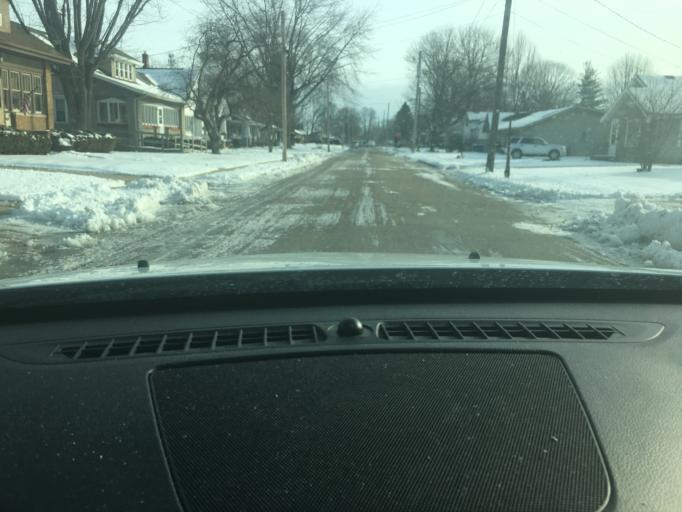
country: US
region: Illinois
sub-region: LaSalle County
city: Peru
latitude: 41.3322
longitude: -89.1290
